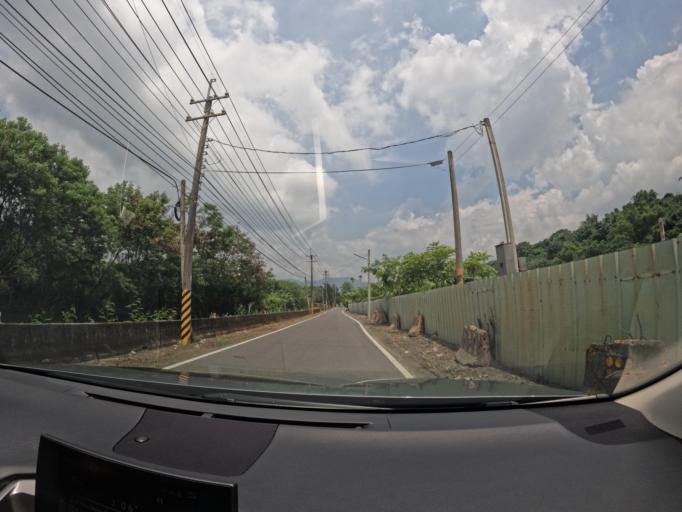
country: TW
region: Taiwan
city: Lugu
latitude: 23.8103
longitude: 120.8205
